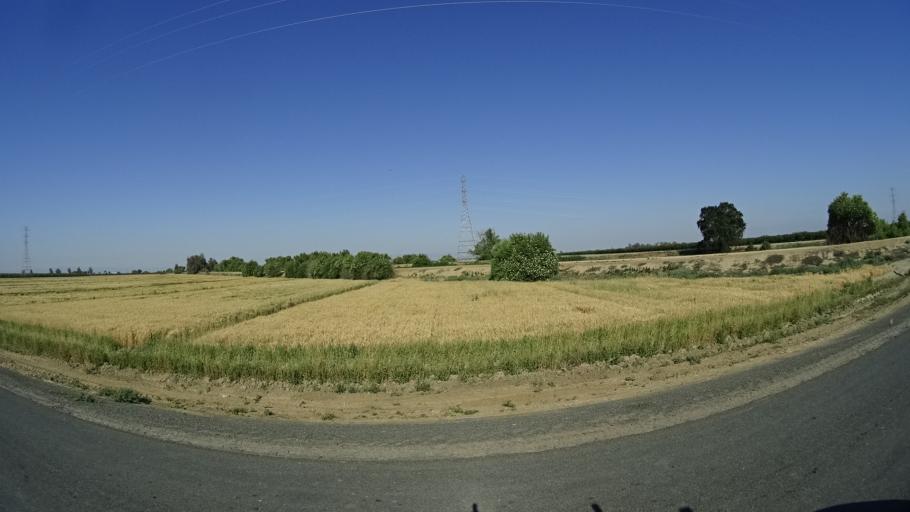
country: US
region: California
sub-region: Fresno County
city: Riverdale
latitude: 36.3732
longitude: -119.8872
